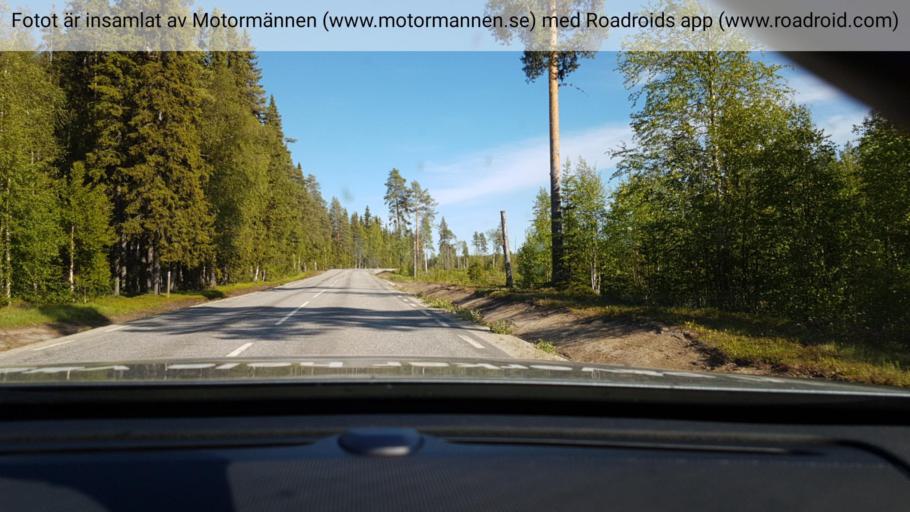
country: SE
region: Vaesterbotten
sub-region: Norsjo Kommun
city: Norsjoe
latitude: 64.6947
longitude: 19.1887
